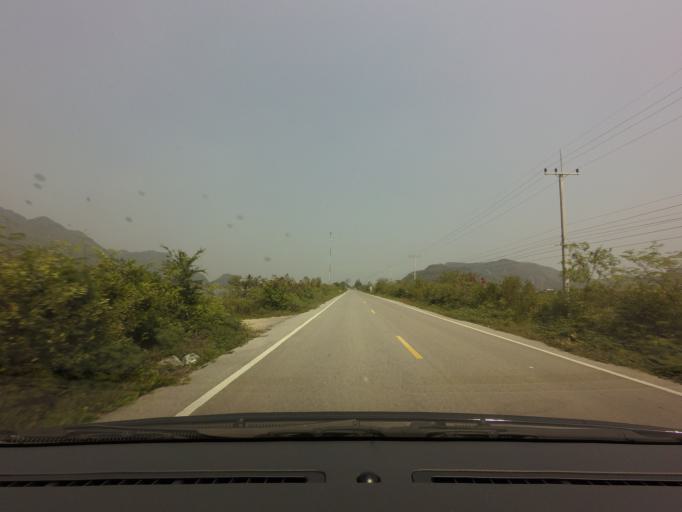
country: TH
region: Prachuap Khiri Khan
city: Sam Roi Yot
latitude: 12.1932
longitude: 99.9784
